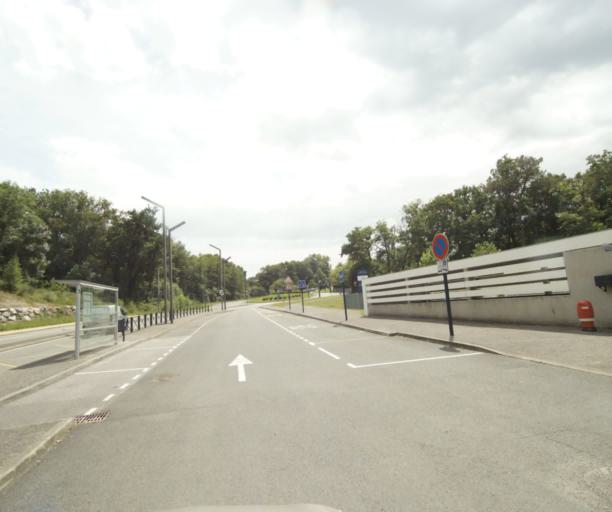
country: FR
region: Aquitaine
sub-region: Departement des Pyrenees-Atlantiques
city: Mouguerre
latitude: 43.4728
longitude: -1.4426
